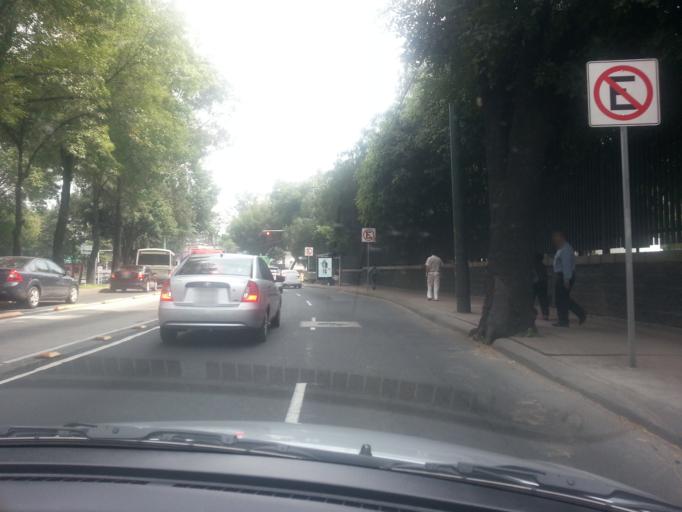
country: MX
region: Mexico City
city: Tlalpan
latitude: 19.2965
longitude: -99.1853
